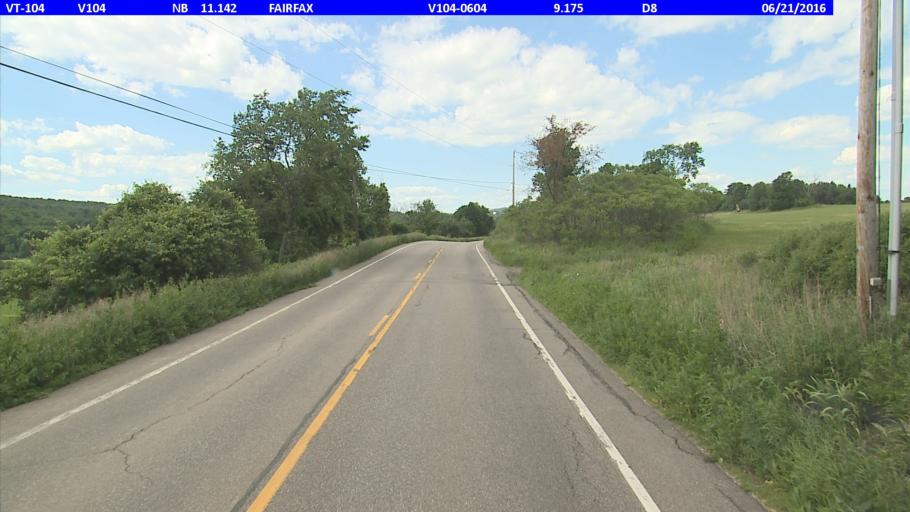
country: US
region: Vermont
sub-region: Franklin County
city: Saint Albans
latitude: 44.7165
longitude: -73.0410
